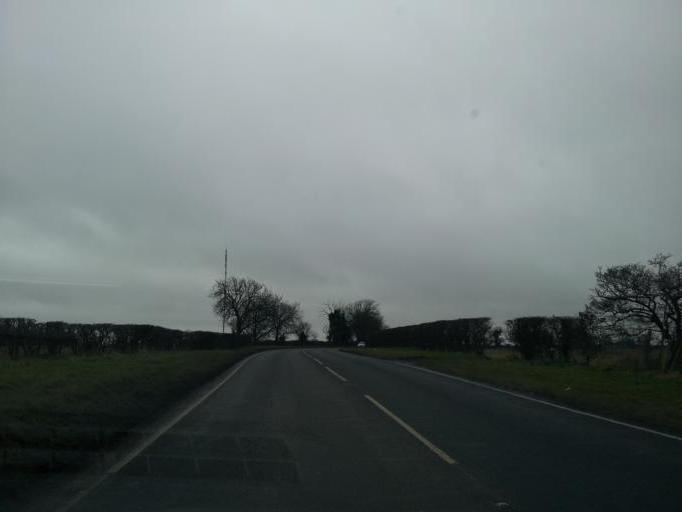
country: GB
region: England
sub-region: Essex
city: Mistley
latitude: 51.9311
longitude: 1.0780
